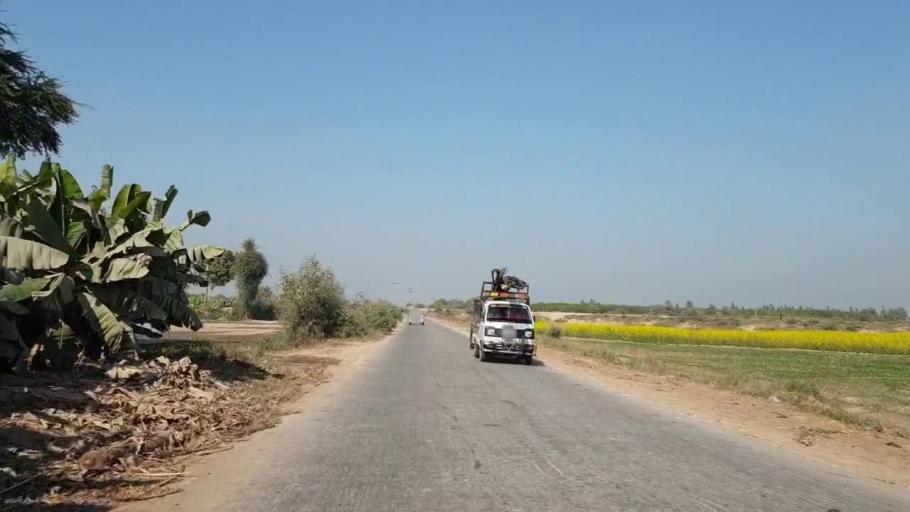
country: PK
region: Sindh
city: Tando Adam
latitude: 25.6482
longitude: 68.5911
